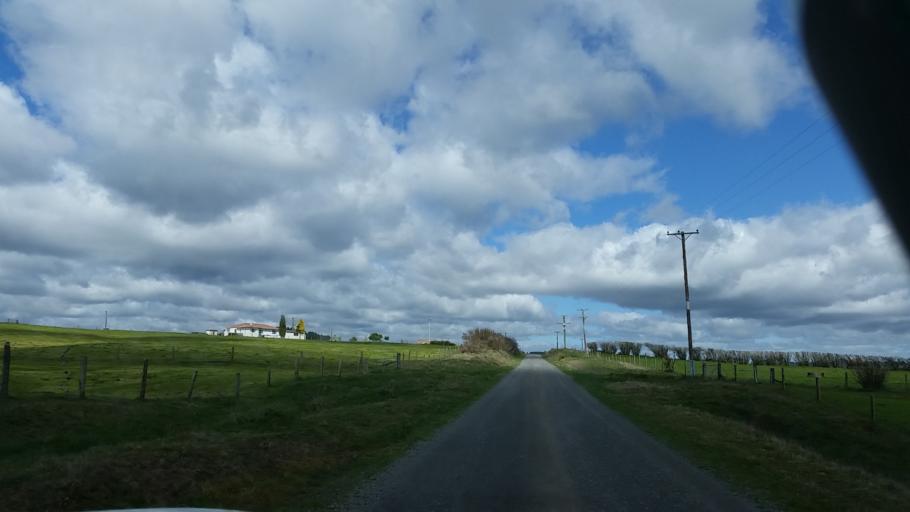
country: NZ
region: Bay of Plenty
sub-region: Whakatane District
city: Murupara
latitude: -38.3081
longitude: 176.5586
